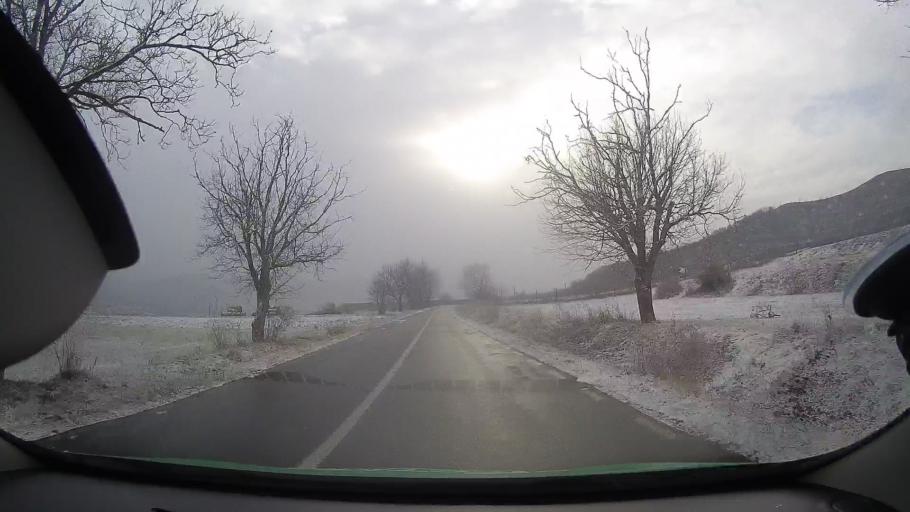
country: RO
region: Alba
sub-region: Comuna Rimetea
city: Rimetea
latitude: 46.4337
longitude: 23.5605
